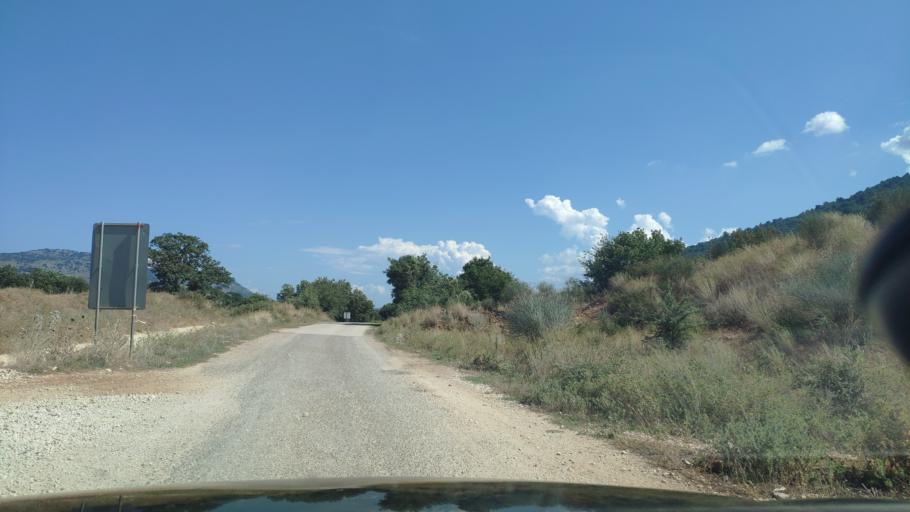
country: GR
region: West Greece
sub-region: Nomos Aitolias kai Akarnanias
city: Katouna
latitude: 38.8511
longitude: 21.0906
